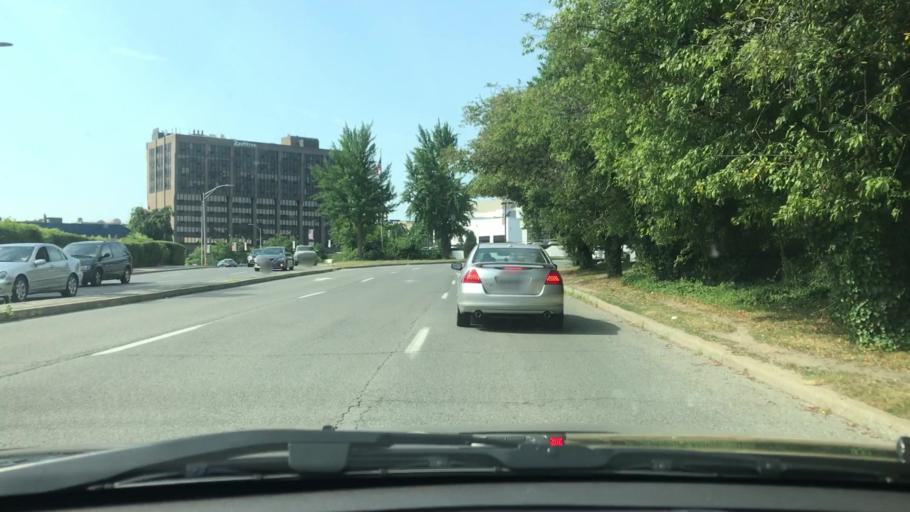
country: US
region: New York
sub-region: Westchester County
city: New Rochelle
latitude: 40.9164
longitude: -73.7781
